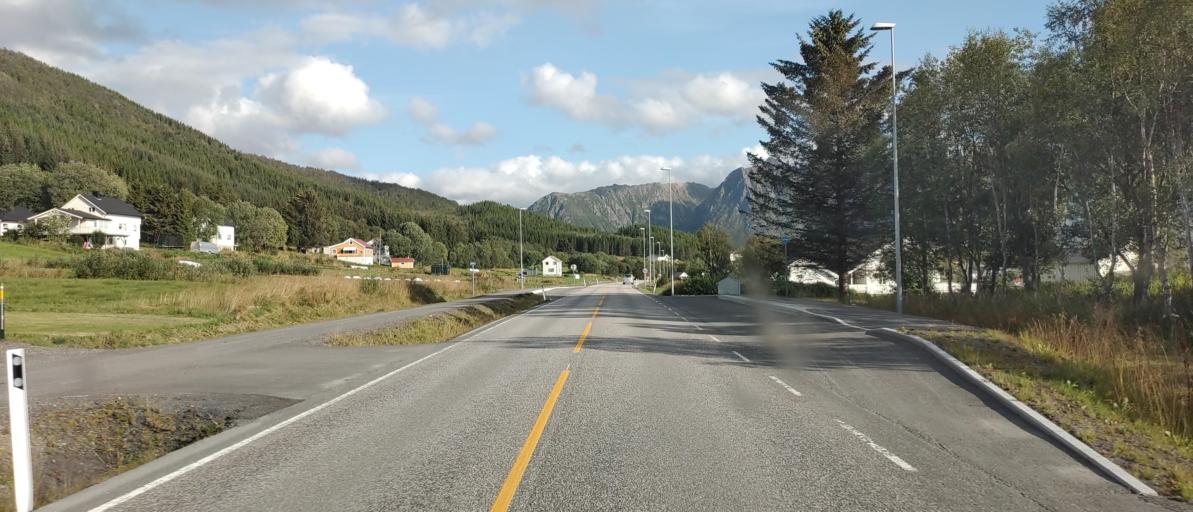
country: NO
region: Nordland
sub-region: Sortland
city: Sortland
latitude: 68.7499
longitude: 15.4936
